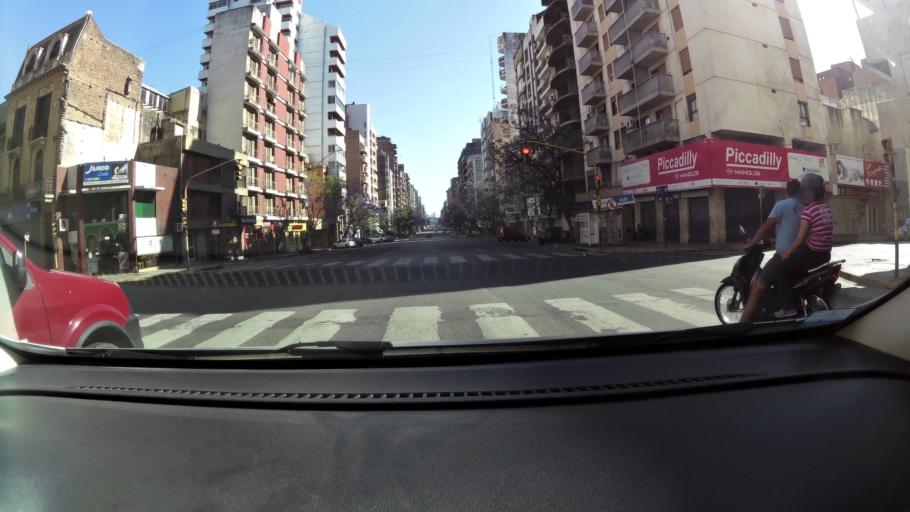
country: AR
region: Cordoba
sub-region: Departamento de Capital
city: Cordoba
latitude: -31.4205
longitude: -64.1815
